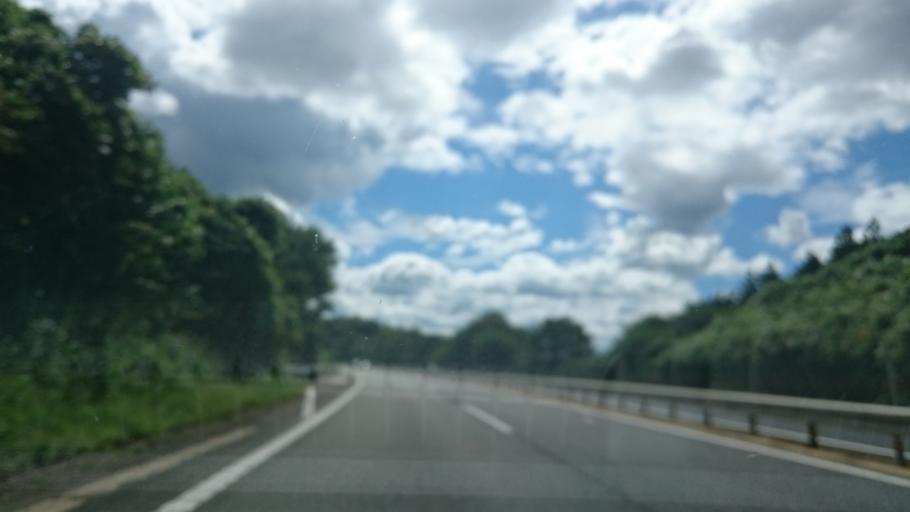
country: JP
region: Gifu
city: Nakatsugawa
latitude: 35.5049
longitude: 137.5292
